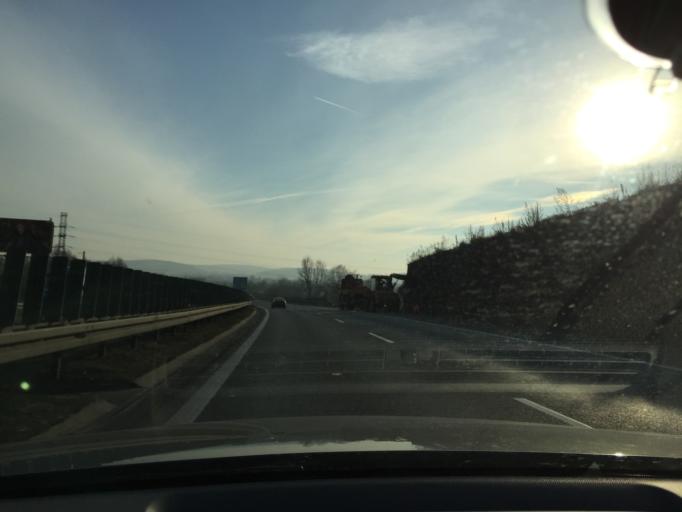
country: PL
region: Lesser Poland Voivodeship
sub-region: Powiat krakowski
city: Kryspinow
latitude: 50.0445
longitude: 19.8069
